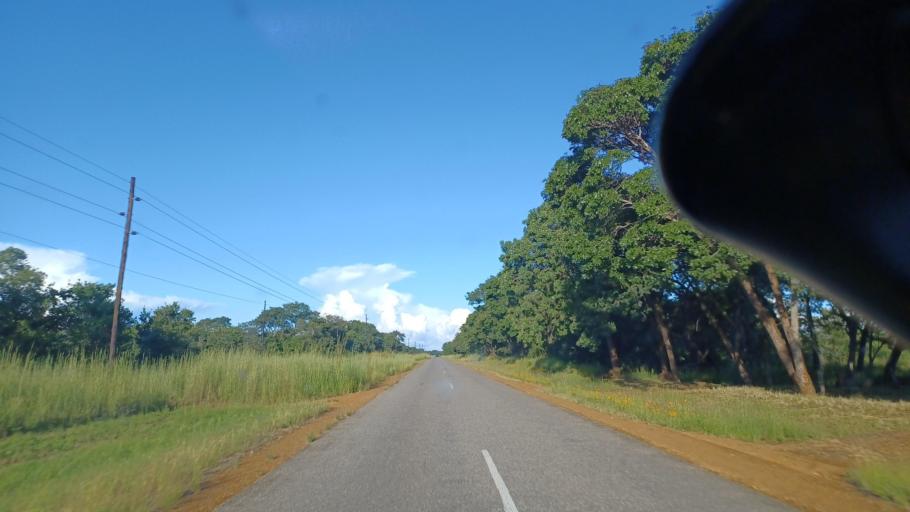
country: ZM
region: North-Western
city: Kalengwa
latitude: -13.2003
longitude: 24.8017
